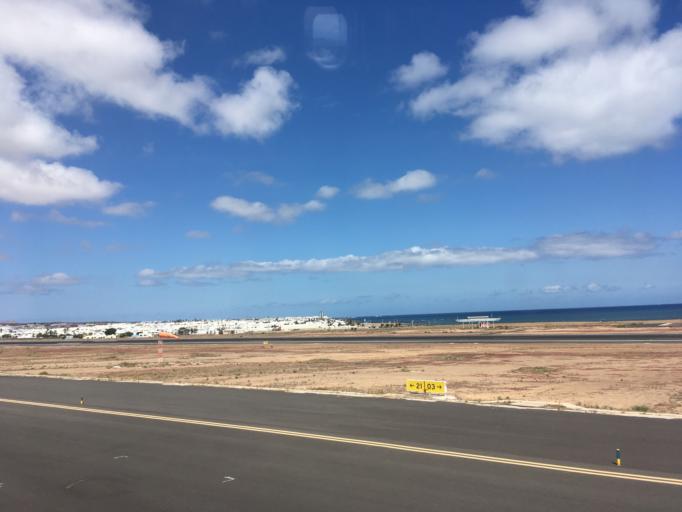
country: ES
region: Canary Islands
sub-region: Provincia de Las Palmas
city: Tias
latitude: 28.9486
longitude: -13.6057
